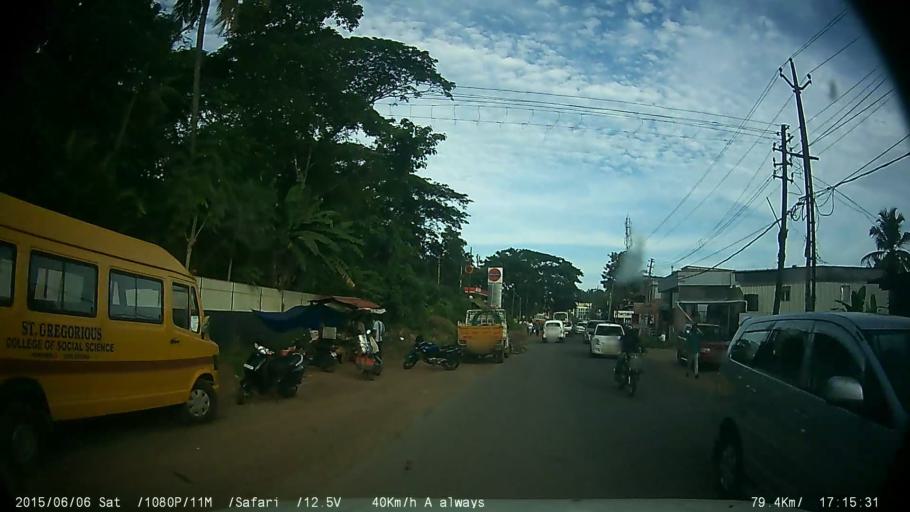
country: IN
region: Kerala
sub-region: Pattanamtitta
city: Tiruvalla
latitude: 9.3952
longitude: 76.5704
